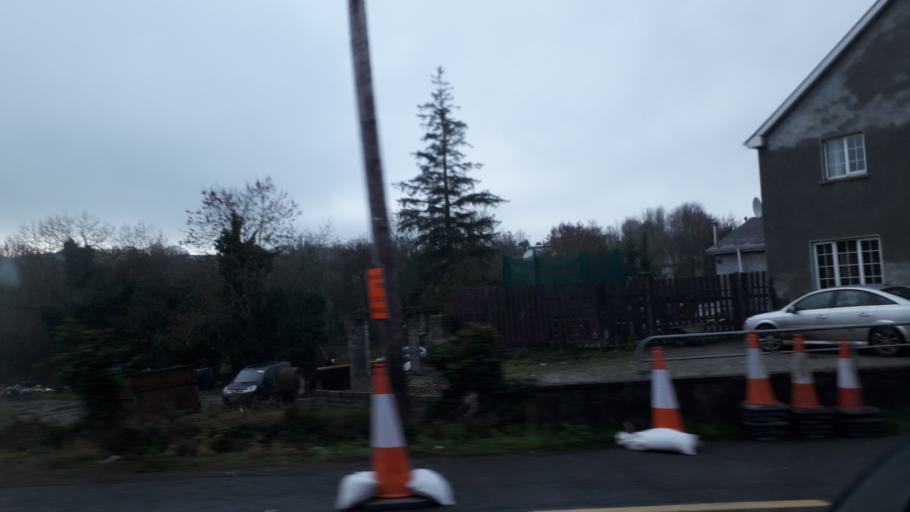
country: IE
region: Ulster
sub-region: County Donegal
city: Raphoe
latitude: 54.9381
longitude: -7.6157
